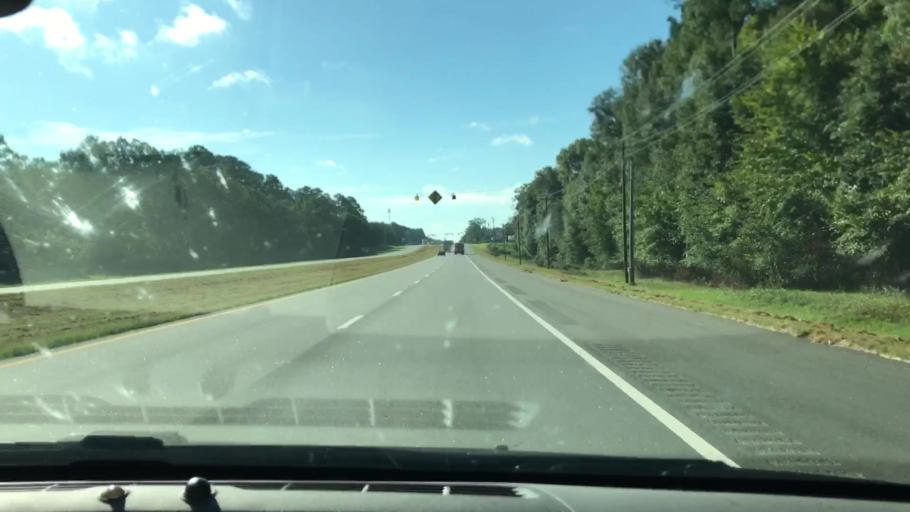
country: US
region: Georgia
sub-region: Lee County
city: Leesburg
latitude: 31.6673
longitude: -84.2843
